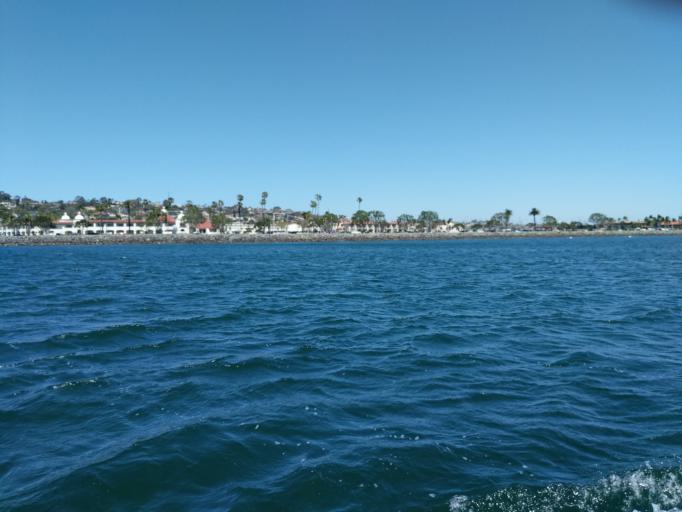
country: US
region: California
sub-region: San Diego County
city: Coronado
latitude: 32.7071
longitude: -117.2302
